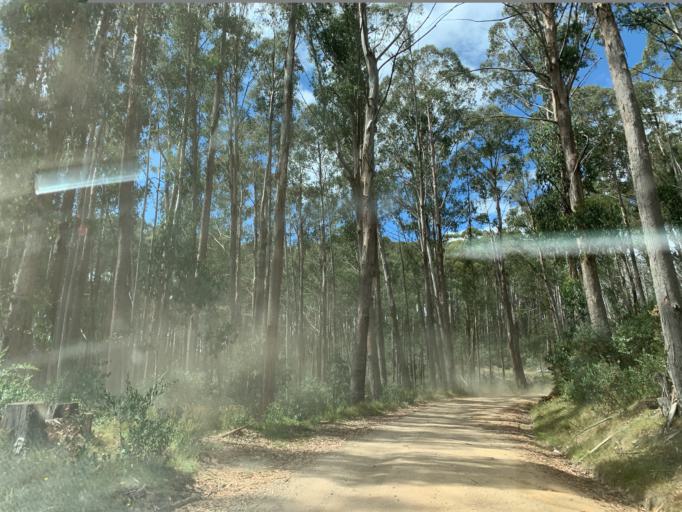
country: AU
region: Victoria
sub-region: Mansfield
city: Mansfield
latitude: -37.0990
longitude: 146.5407
